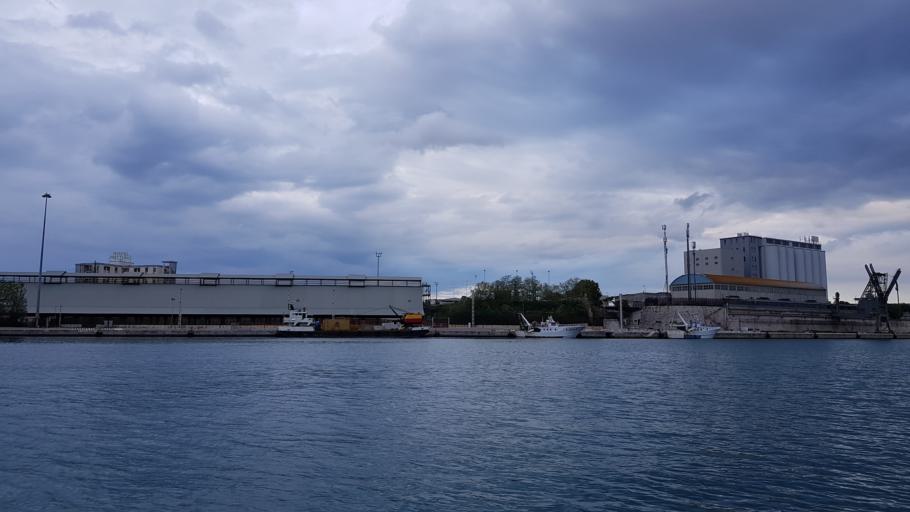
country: IT
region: Apulia
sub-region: Provincia di Brindisi
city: Brindisi
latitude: 40.6404
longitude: 17.9496
